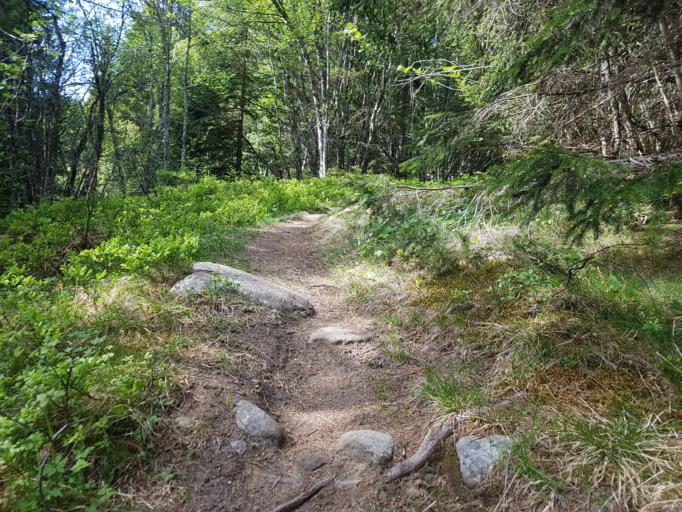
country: NO
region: Sor-Trondelag
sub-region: Trondheim
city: Trondheim
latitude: 63.4248
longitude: 10.3346
